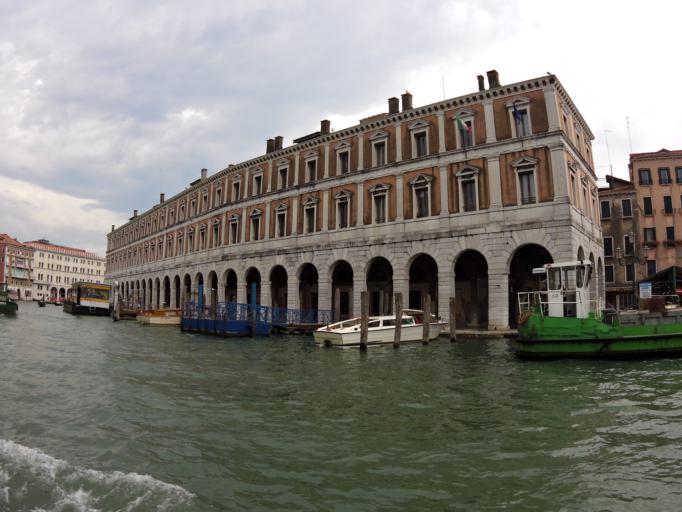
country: IT
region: Veneto
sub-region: Provincia di Venezia
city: Venice
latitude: 45.4398
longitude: 12.3347
